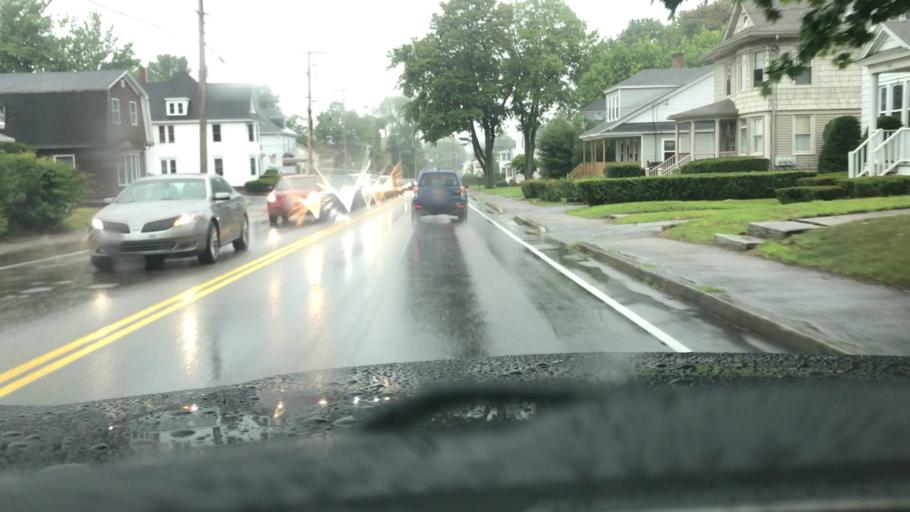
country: US
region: Maine
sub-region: York County
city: Biddeford
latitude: 43.4859
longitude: -70.4685
